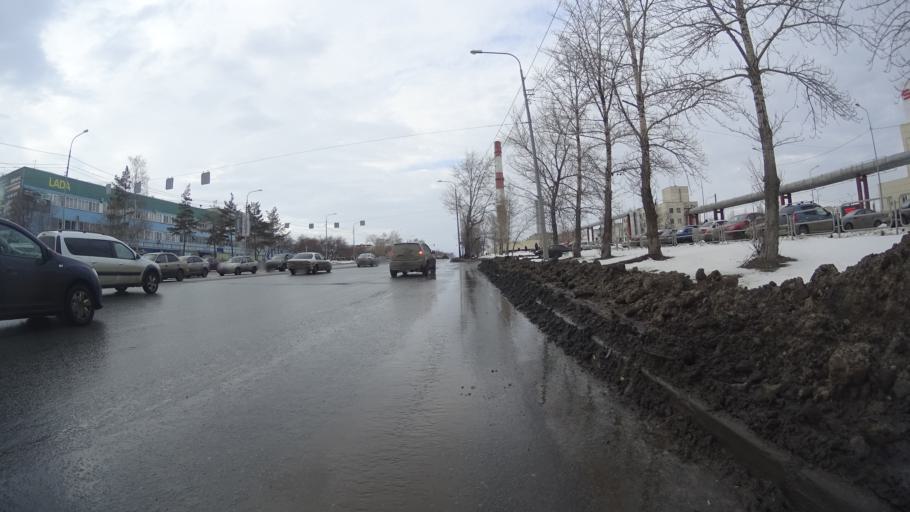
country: RU
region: Chelyabinsk
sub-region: Gorod Chelyabinsk
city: Chelyabinsk
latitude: 55.2039
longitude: 61.3242
